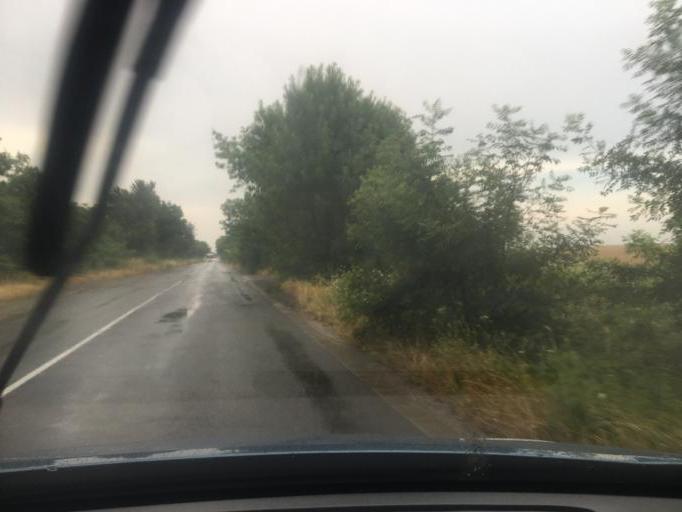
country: BG
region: Burgas
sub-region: Obshtina Burgas
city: Burgas
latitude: 42.5583
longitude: 27.4914
